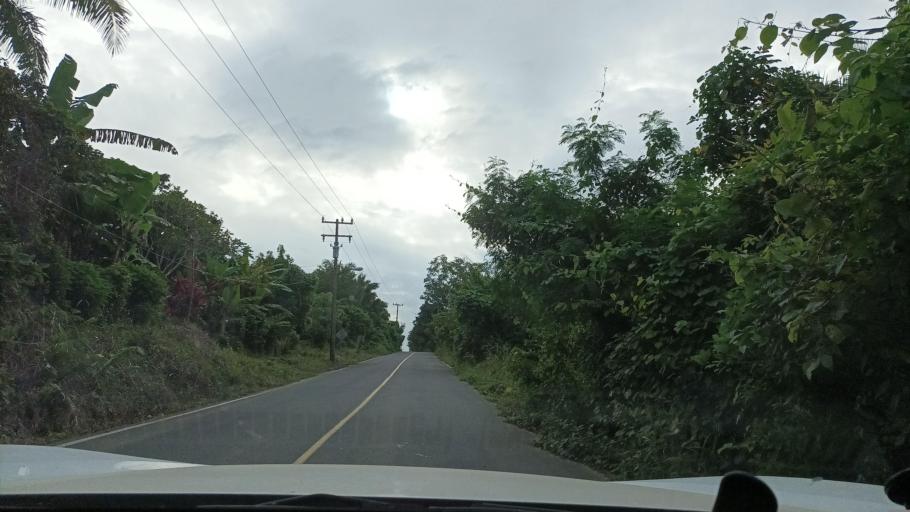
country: MX
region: Veracruz
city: Hidalgotitlan
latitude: 17.7187
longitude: -94.4788
